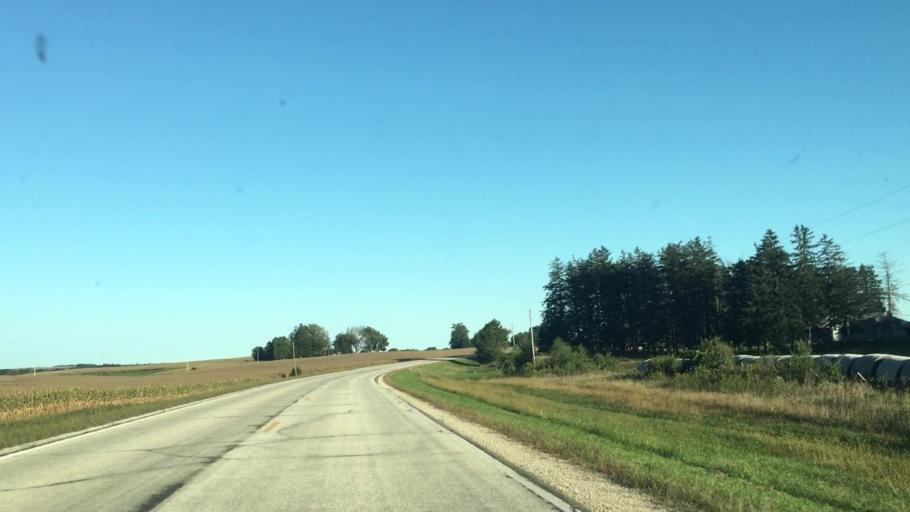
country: US
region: Minnesota
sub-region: Fillmore County
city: Chatfield
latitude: 43.8393
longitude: -92.0774
